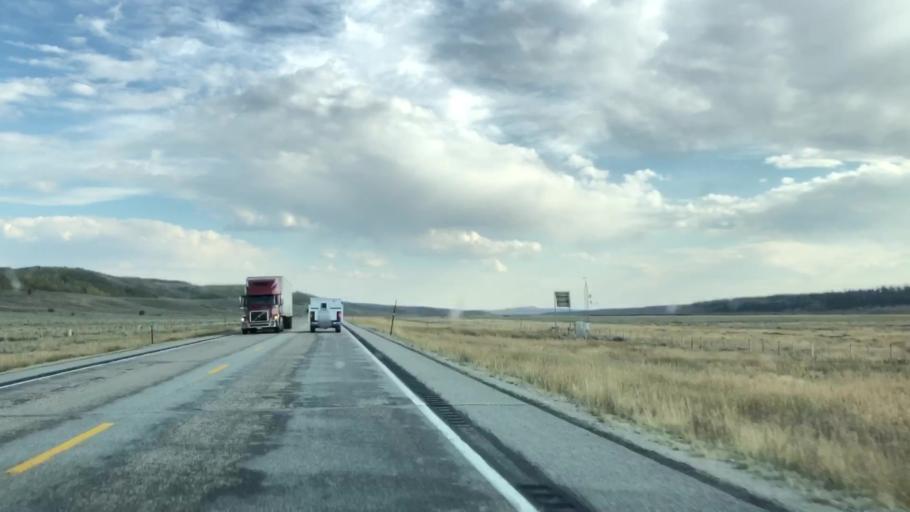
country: US
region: Wyoming
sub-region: Sublette County
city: Pinedale
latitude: 43.1064
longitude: -110.1717
